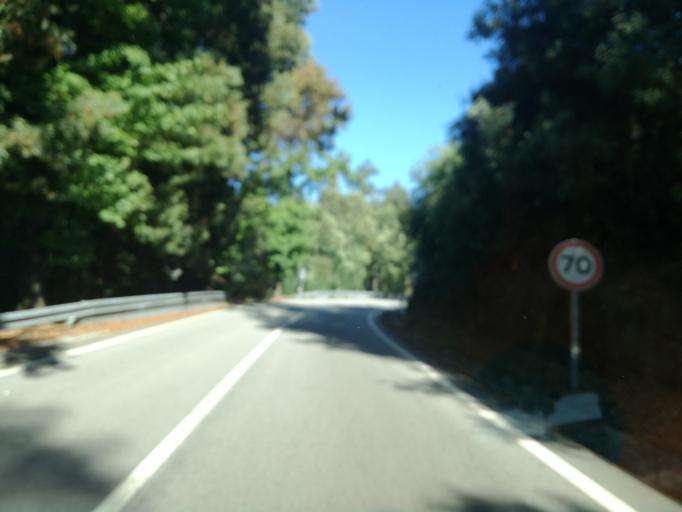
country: PT
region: Porto
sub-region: Pacos de Ferreira
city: Seroa
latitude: 41.2564
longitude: -8.4632
